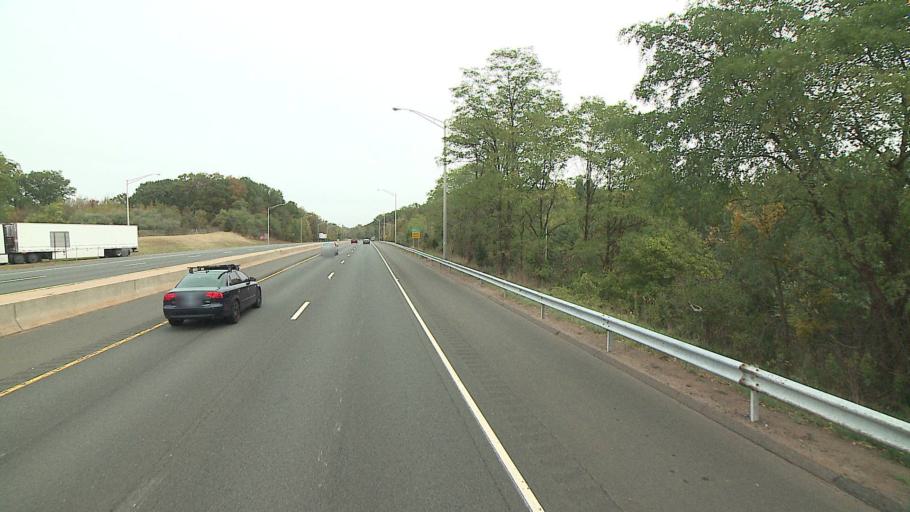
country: US
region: Connecticut
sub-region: Hartford County
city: Newington
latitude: 41.7001
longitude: -72.7578
